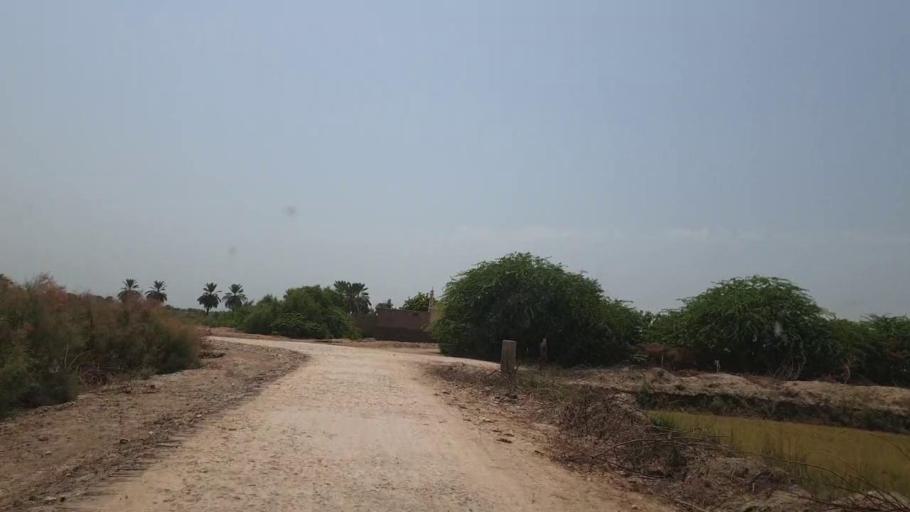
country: PK
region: Sindh
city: Garhi Yasin
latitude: 27.8504
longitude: 68.5875
